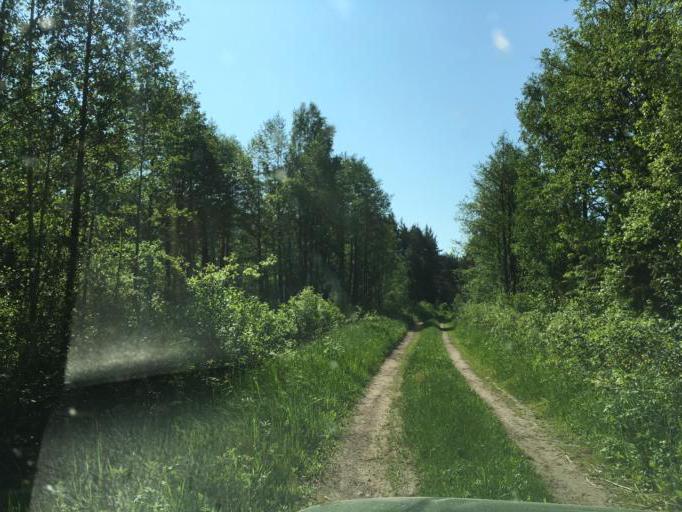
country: LV
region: Ventspils
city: Ventspils
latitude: 57.4766
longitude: 21.7634
